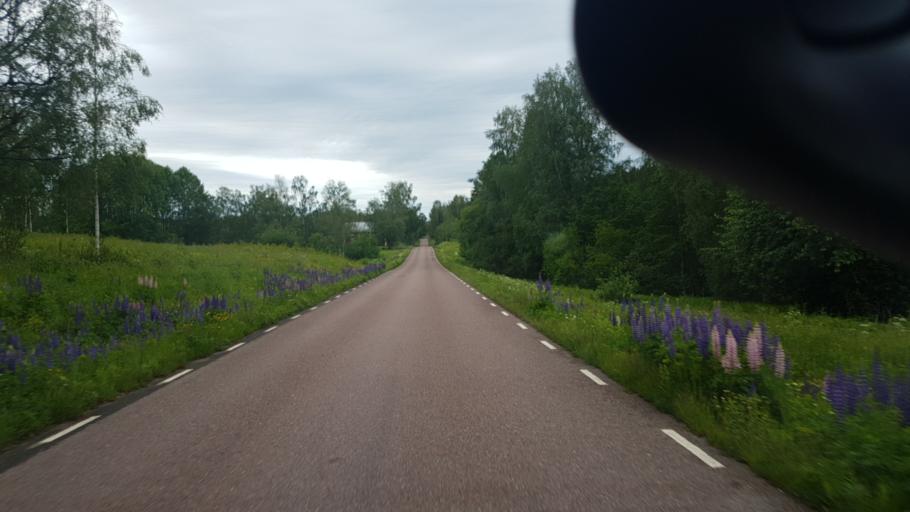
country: NO
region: Ostfold
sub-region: Romskog
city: Romskog
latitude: 59.7344
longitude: 12.0613
